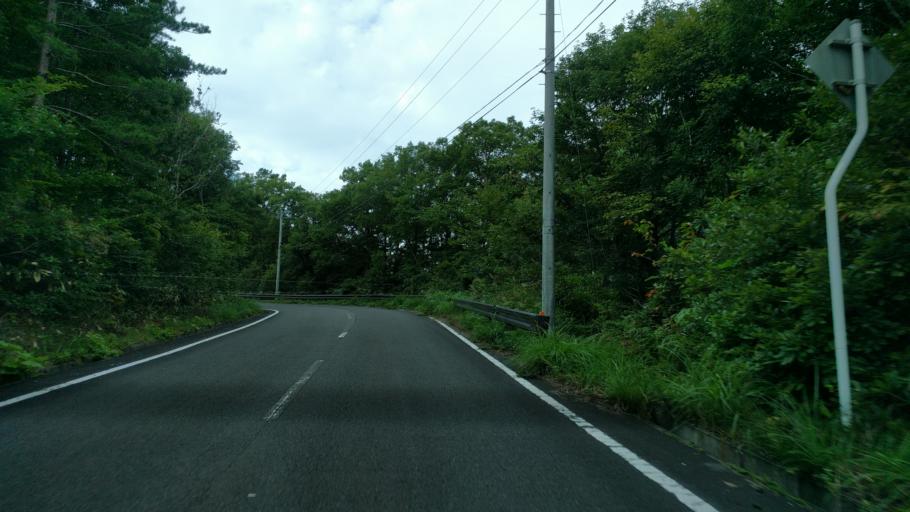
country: JP
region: Fukushima
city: Kitakata
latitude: 37.5152
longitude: 139.7599
